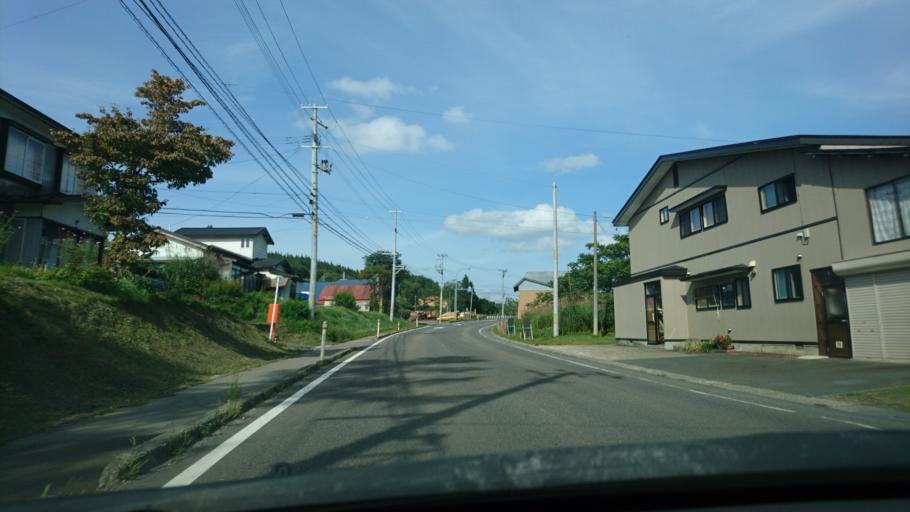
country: JP
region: Akita
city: Yokotemachi
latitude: 39.2997
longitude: 140.7360
